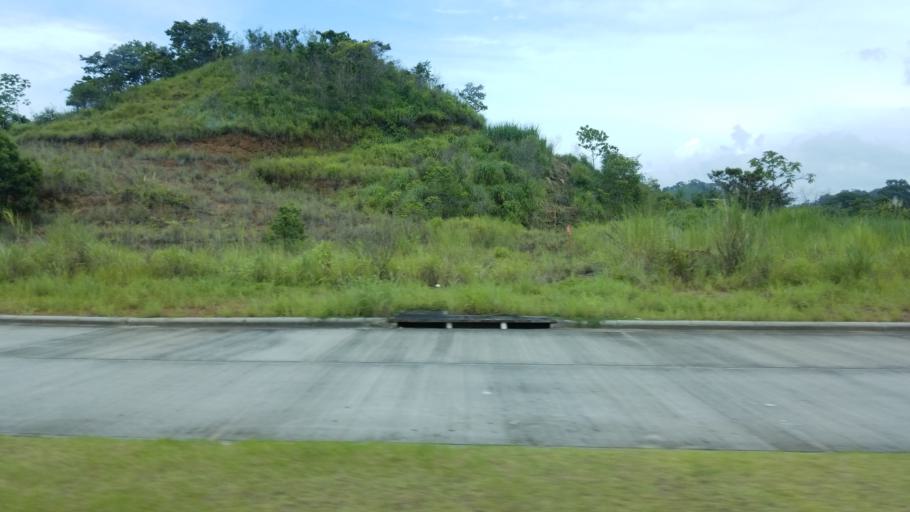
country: PA
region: Panama
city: Las Cumbres
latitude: 9.1083
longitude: -79.4752
